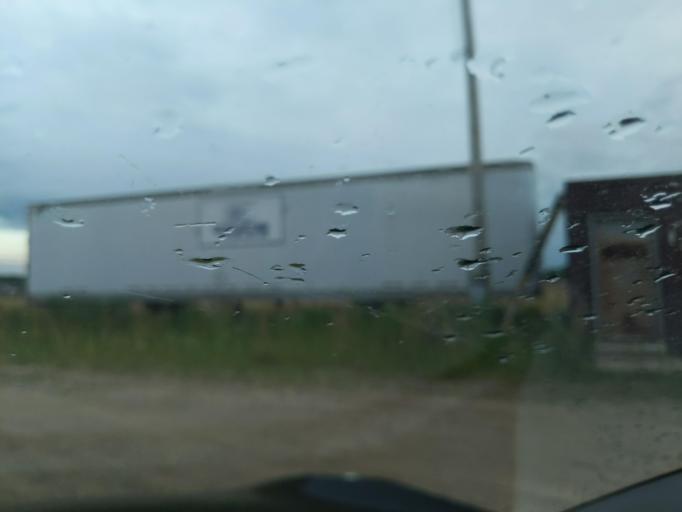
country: US
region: Michigan
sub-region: Clinton County
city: DeWitt
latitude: 42.8130
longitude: -84.6000
